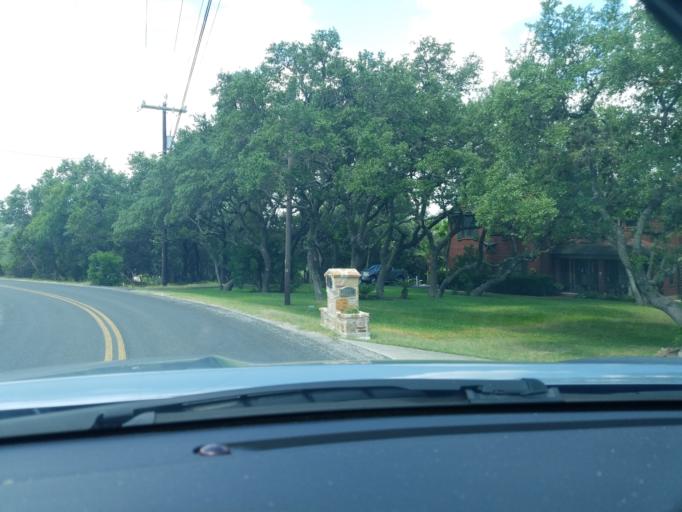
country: US
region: Texas
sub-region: Bexar County
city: Timberwood Park
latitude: 29.6931
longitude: -98.4902
